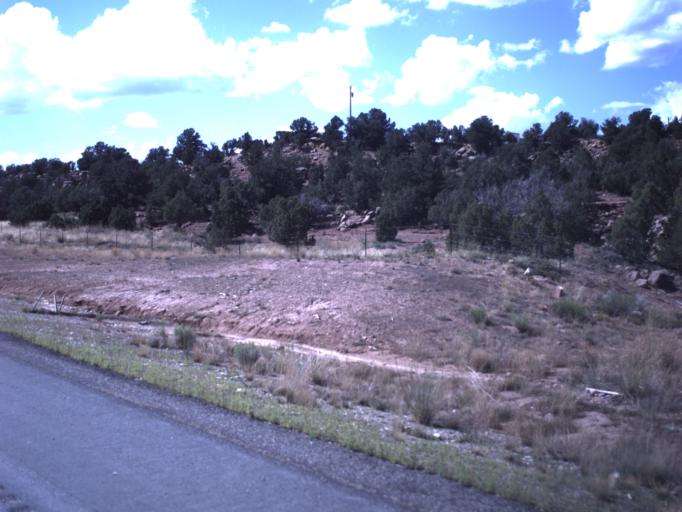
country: US
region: Utah
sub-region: Duchesne County
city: Duchesne
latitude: 40.2037
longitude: -110.7940
